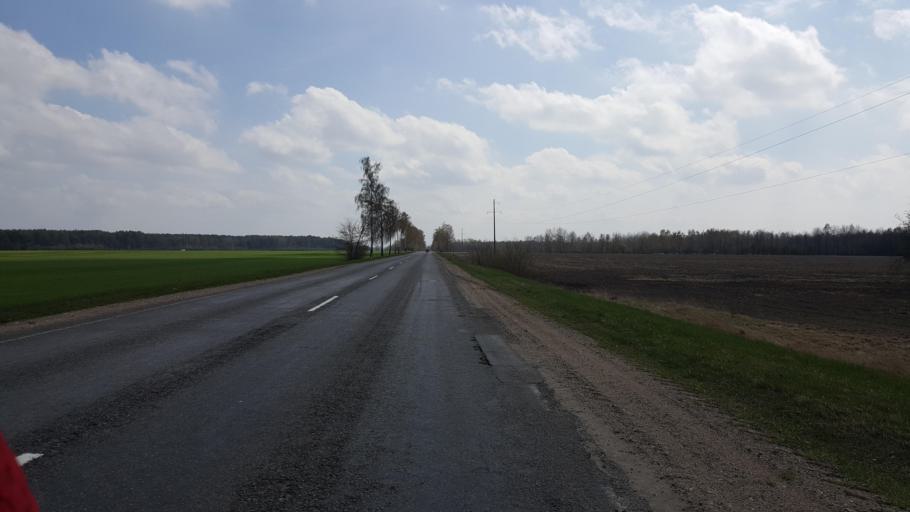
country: BY
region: Brest
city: Zhabinka
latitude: 52.2523
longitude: 23.9687
